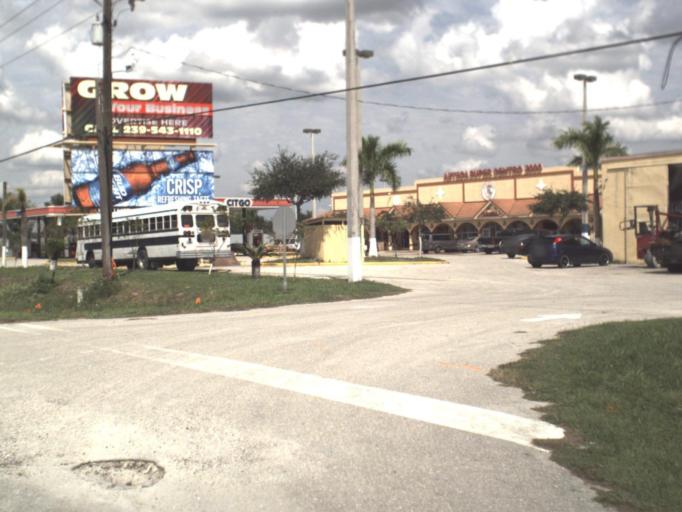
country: US
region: Florida
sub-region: Hendry County
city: LaBelle
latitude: 26.6990
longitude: -81.4371
